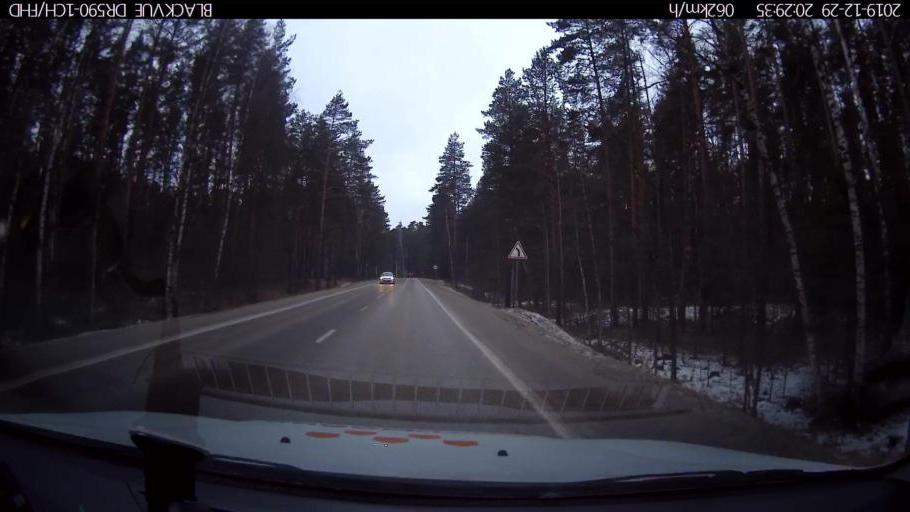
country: RU
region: Nizjnij Novgorod
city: Afonino
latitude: 56.1796
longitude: 44.1012
